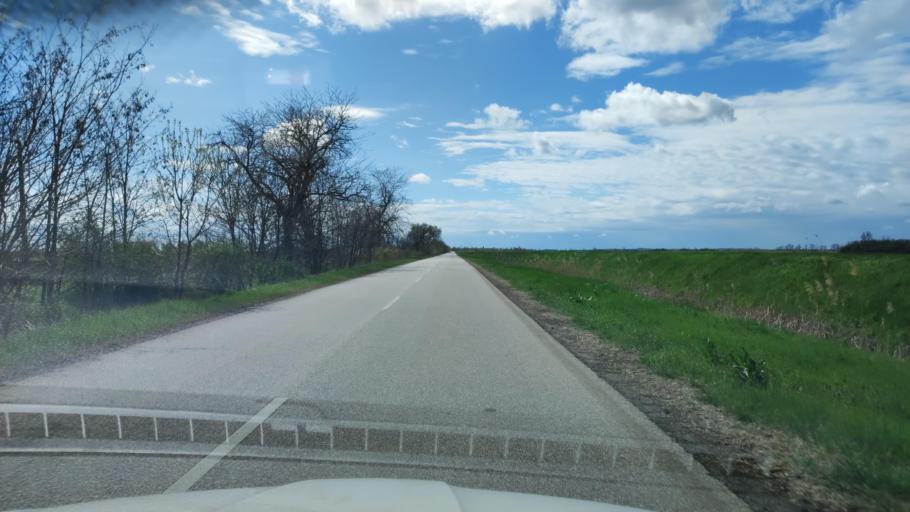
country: HU
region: Pest
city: Abony
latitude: 47.1395
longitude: 20.0116
